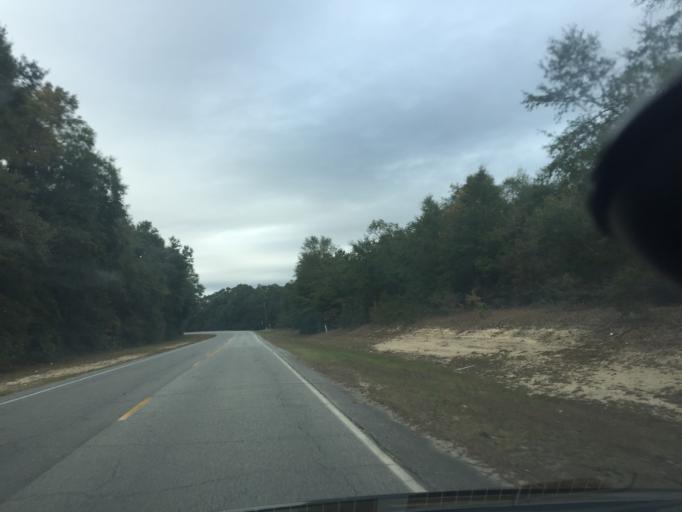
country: US
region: Georgia
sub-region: Chatham County
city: Bloomingdale
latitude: 32.1083
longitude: -81.3841
